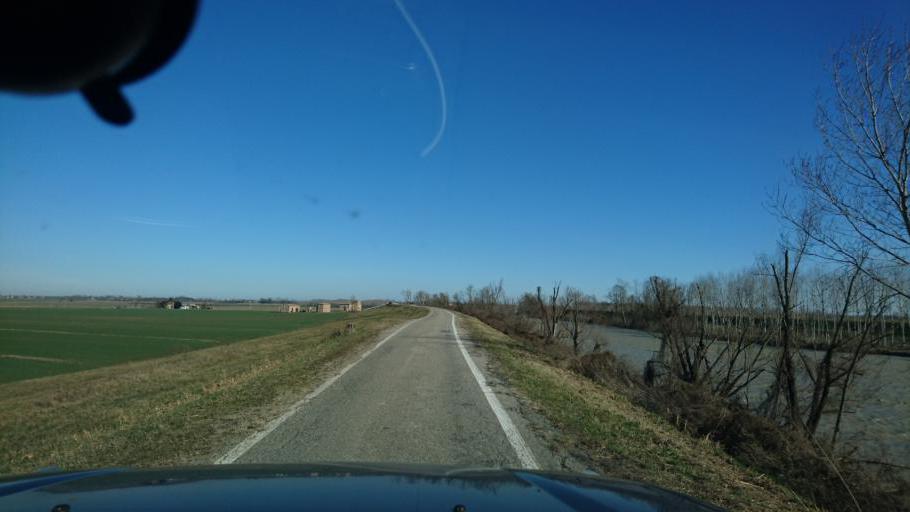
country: IT
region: Veneto
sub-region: Provincia di Rovigo
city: Ariano
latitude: 44.9386
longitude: 12.1602
